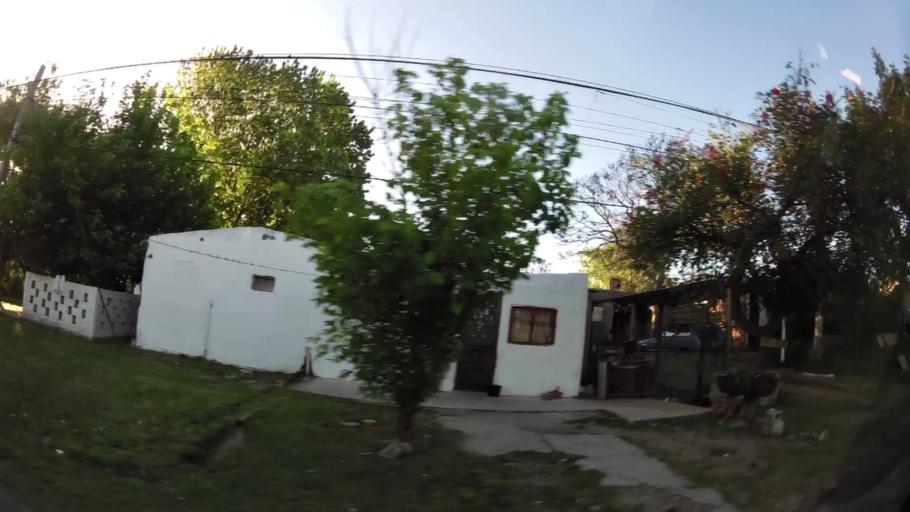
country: UY
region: Montevideo
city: Montevideo
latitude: -34.8383
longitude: -56.1980
